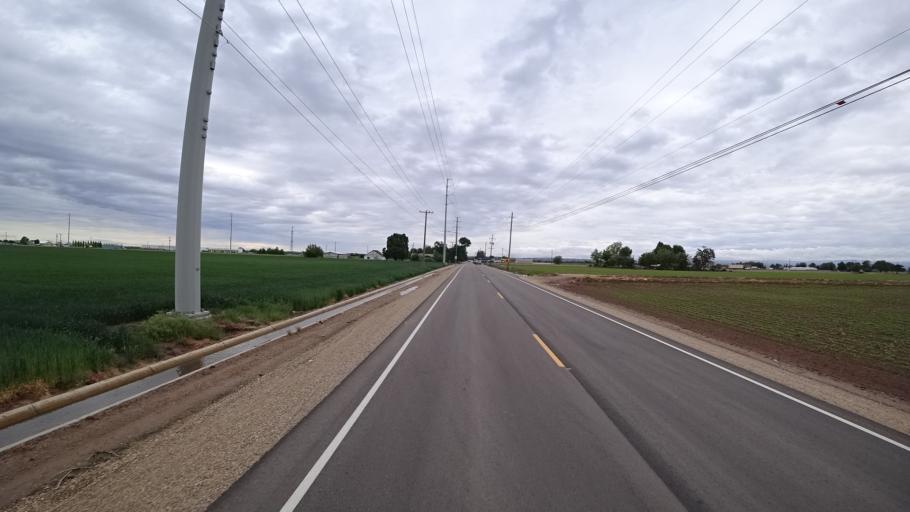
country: US
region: Idaho
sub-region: Ada County
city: Star
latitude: 43.6609
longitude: -116.5130
